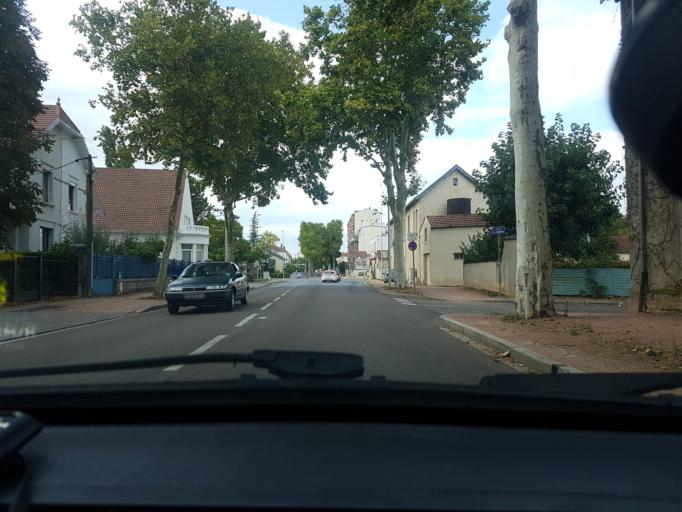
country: FR
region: Bourgogne
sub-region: Departement de la Cote-d'Or
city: Longvic
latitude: 47.3046
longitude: 5.0498
